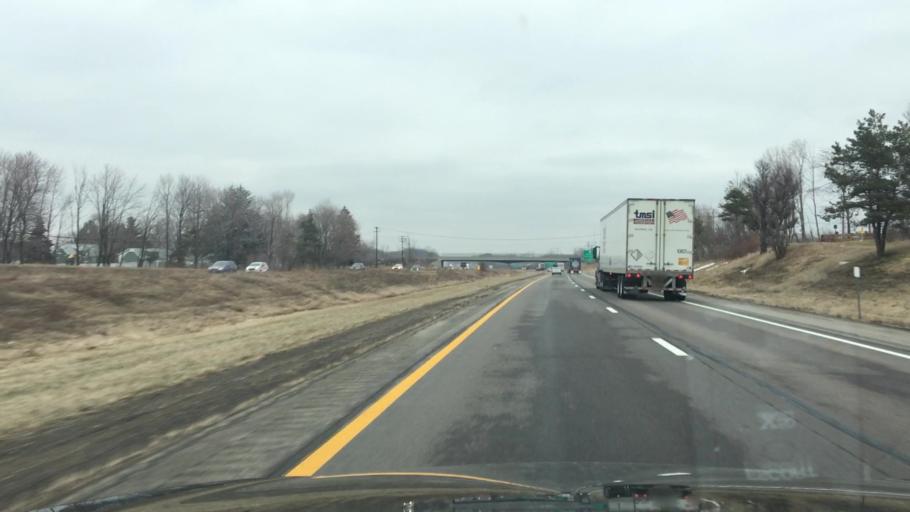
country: US
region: New York
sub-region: Erie County
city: Wanakah
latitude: 42.7310
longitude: -78.8683
